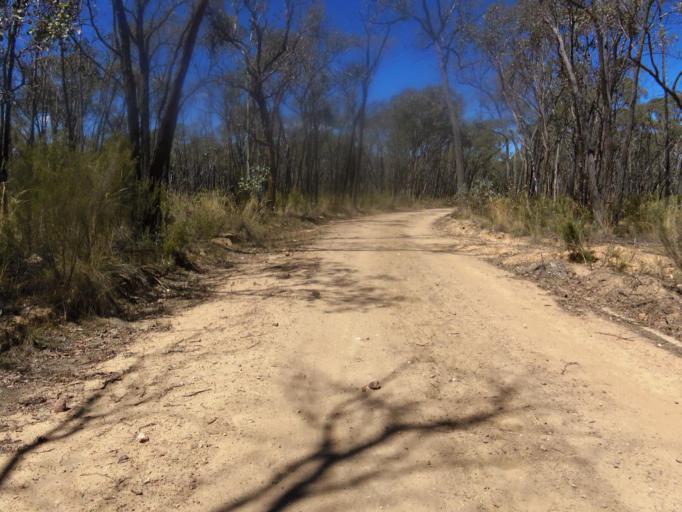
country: AU
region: Victoria
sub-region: Mount Alexander
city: Castlemaine
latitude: -37.0115
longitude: 144.1268
